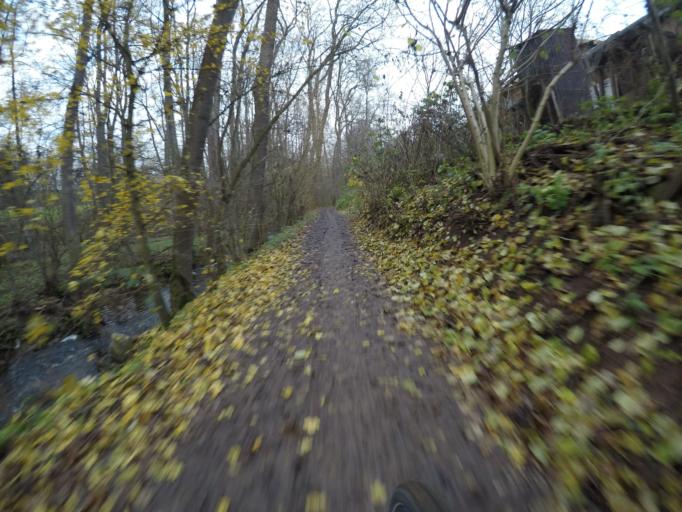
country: DE
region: Baden-Wuerttemberg
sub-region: Regierungsbezirk Stuttgart
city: Ostfildern
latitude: 48.7071
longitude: 9.2179
